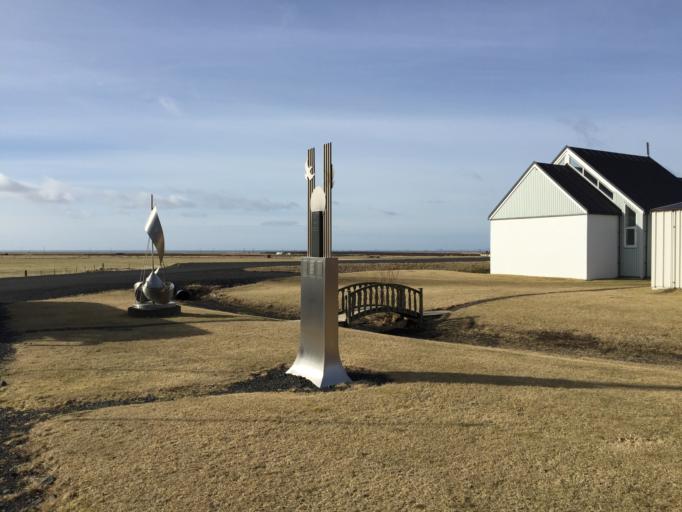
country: IS
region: South
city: Vestmannaeyjar
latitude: 63.5261
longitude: -19.4920
